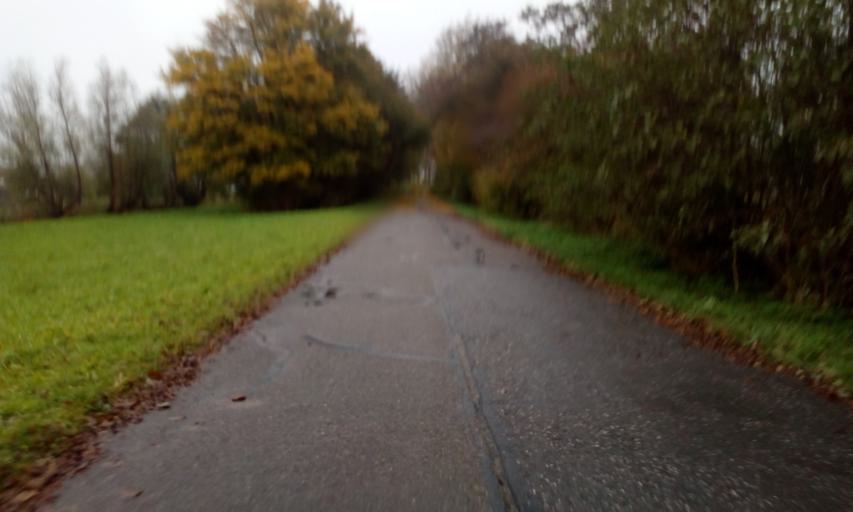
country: NL
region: South Holland
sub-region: Gemeente Lansingerland
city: Bergschenhoek
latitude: 51.9705
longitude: 4.4890
